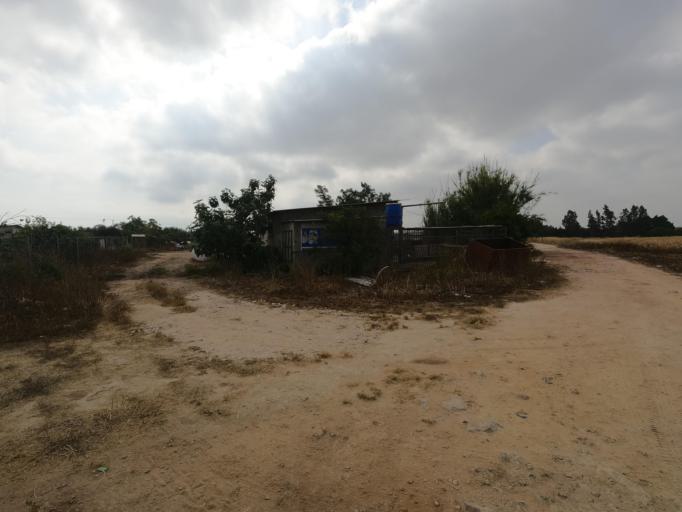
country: CY
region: Ammochostos
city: Deryneia
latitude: 35.0598
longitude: 33.9391
